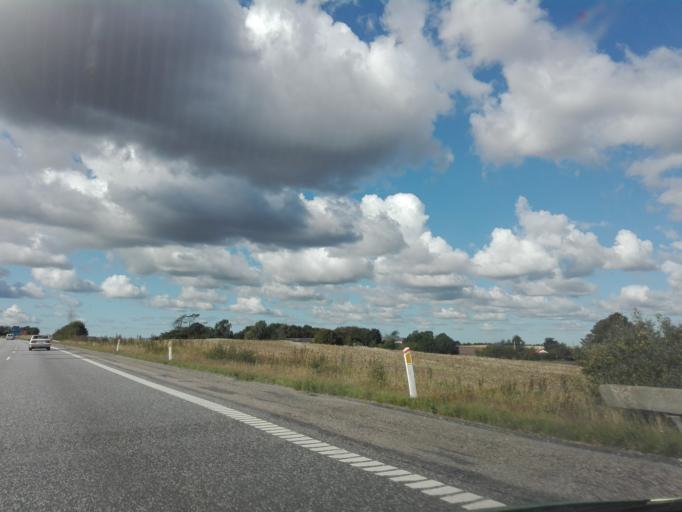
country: DK
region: North Denmark
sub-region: Mariagerfjord Kommune
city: Hobro
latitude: 56.5750
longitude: 9.8417
